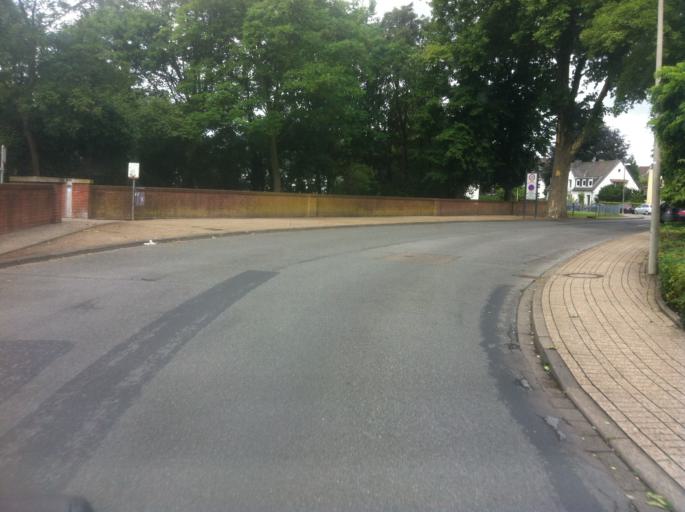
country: DE
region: North Rhine-Westphalia
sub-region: Regierungsbezirk Dusseldorf
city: Emmerich
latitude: 51.8322
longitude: 6.2507
